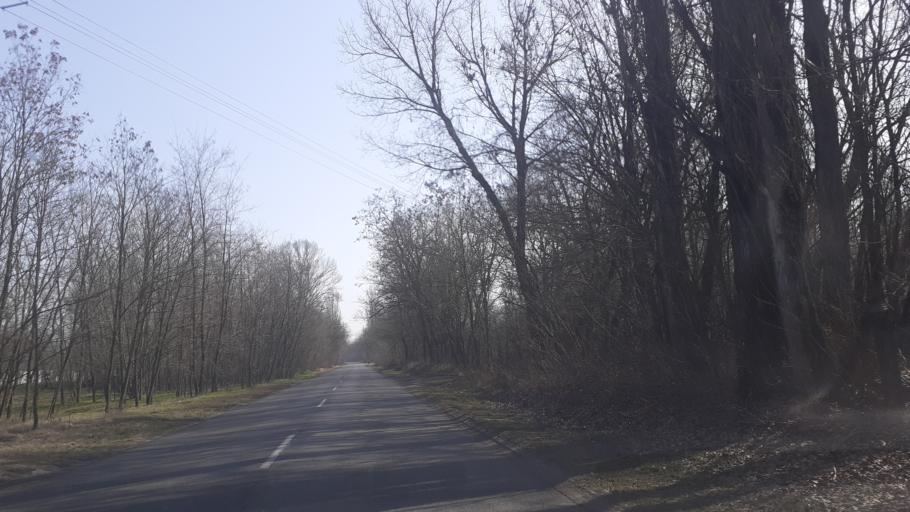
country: HU
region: Bacs-Kiskun
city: Lajosmizse
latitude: 46.9963
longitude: 19.5339
